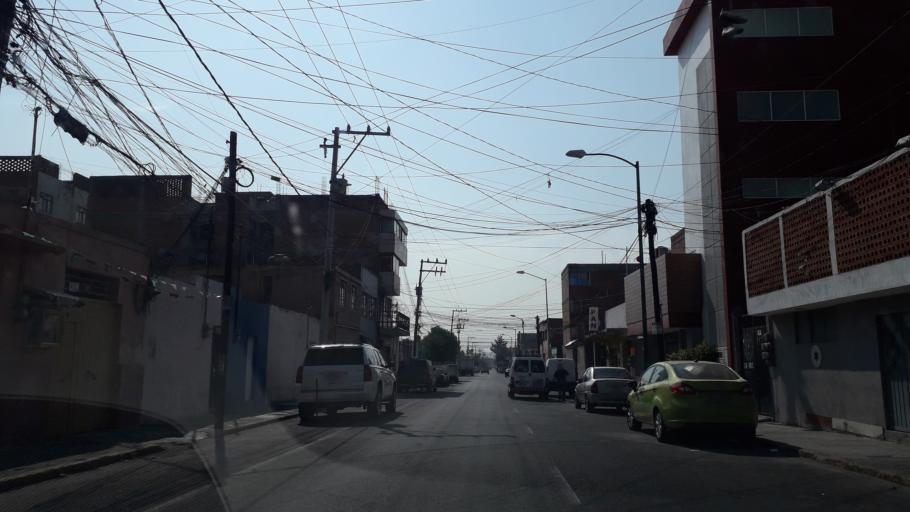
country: MX
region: Puebla
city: Puebla
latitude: 19.0449
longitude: -98.2189
